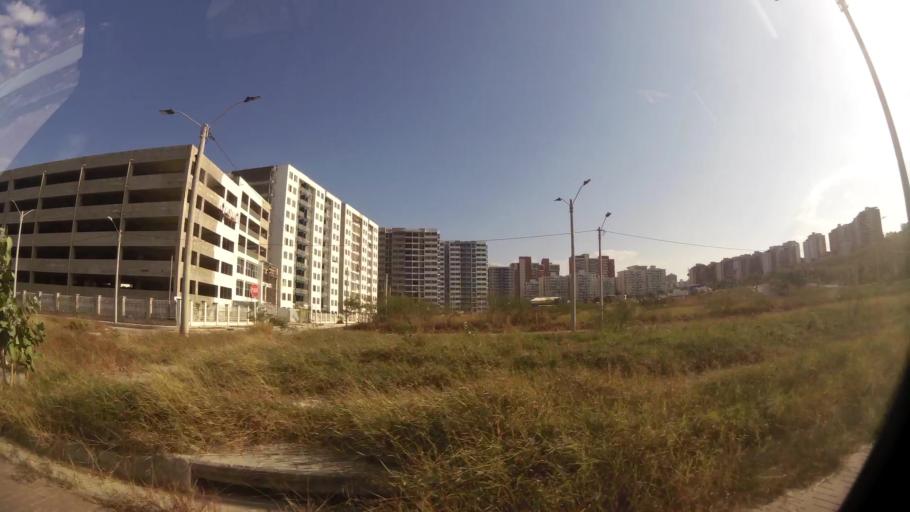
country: CO
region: Atlantico
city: Barranquilla
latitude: 11.0054
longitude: -74.8385
